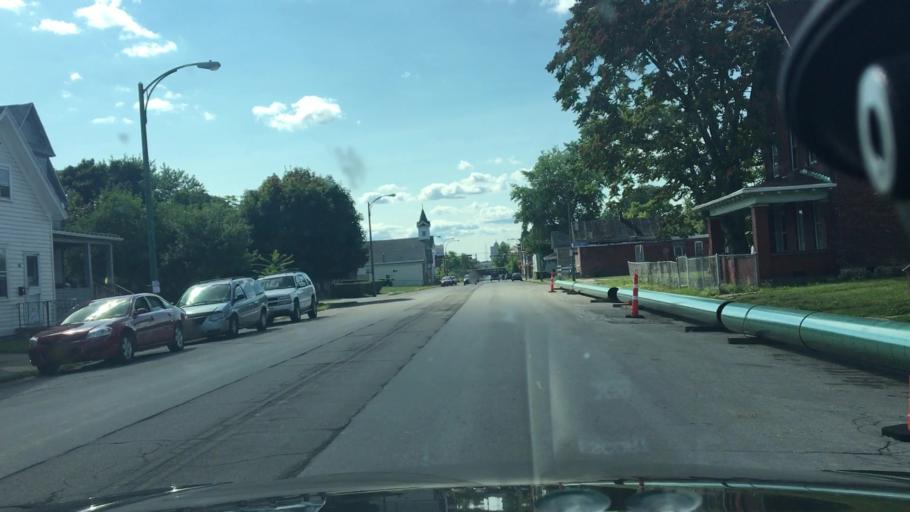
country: US
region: New York
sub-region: Erie County
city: Buffalo
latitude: 42.8798
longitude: -78.8418
